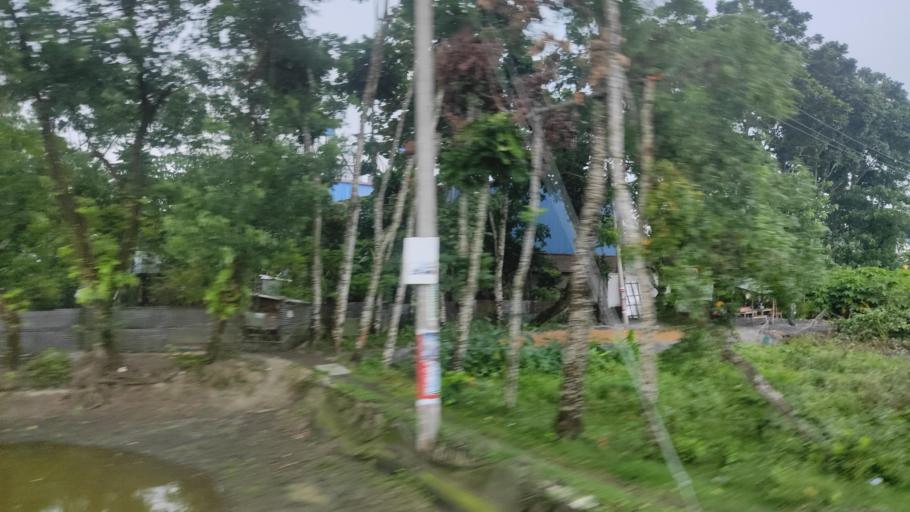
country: BD
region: Barisal
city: Bhandaria
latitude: 22.3094
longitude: 90.3249
